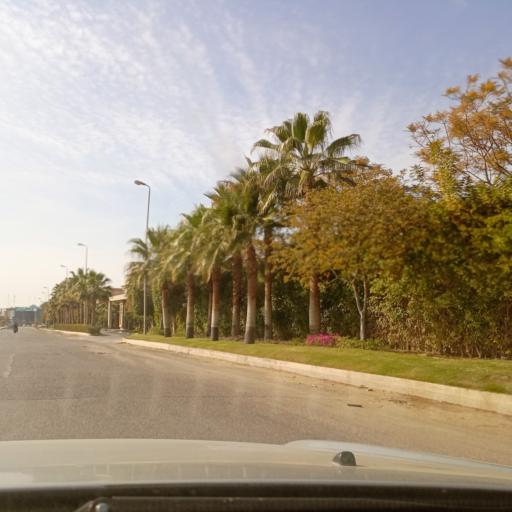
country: EG
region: Muhafazat al Qalyubiyah
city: Al Khankah
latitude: 30.0459
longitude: 31.4902
